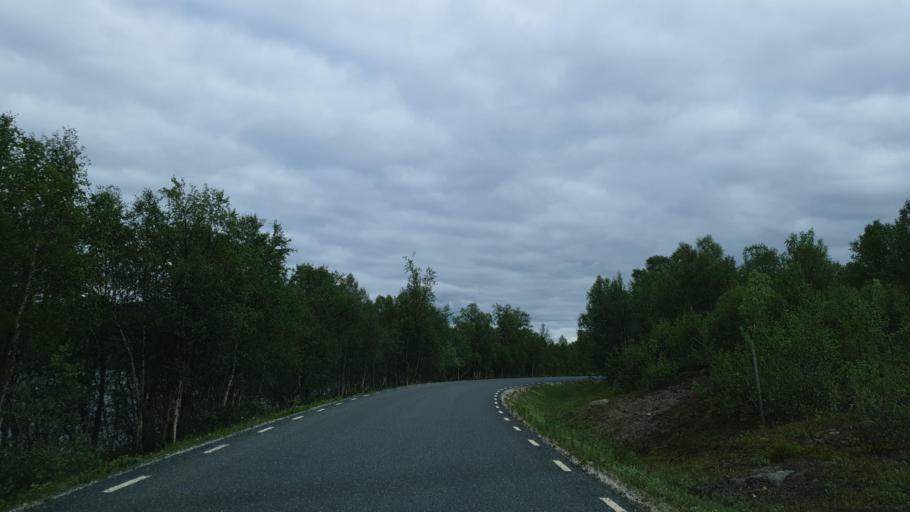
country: NO
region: Nordland
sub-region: Hattfjelldal
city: Hattfjelldal
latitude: 65.4210
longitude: 14.9145
